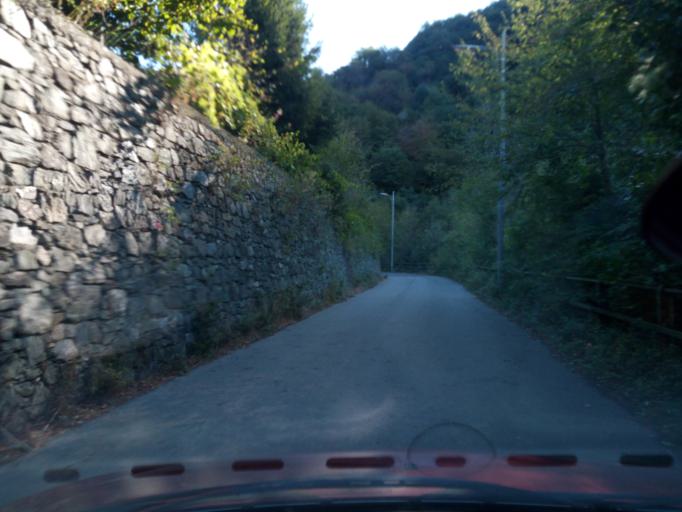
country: IT
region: Liguria
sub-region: Provincia di Genova
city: Isoverde
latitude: 44.4820
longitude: 8.8365
